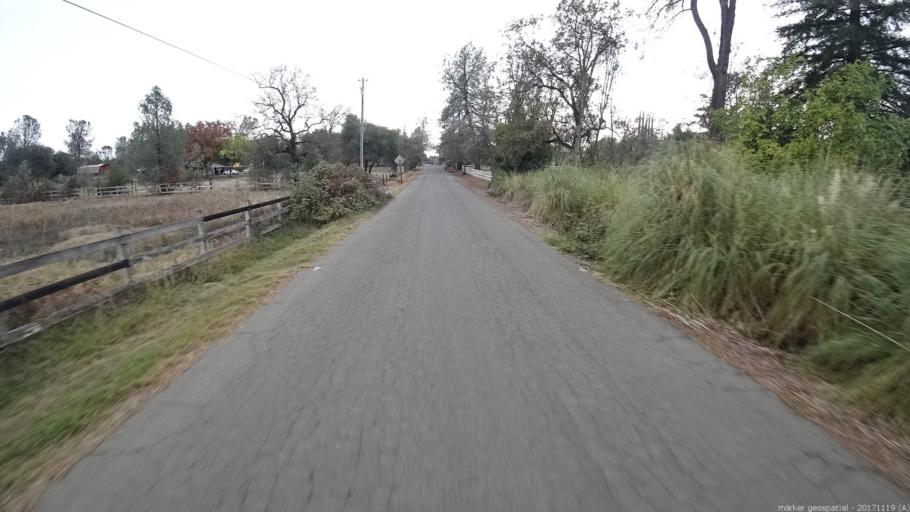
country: US
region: California
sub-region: Shasta County
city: Shasta
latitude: 40.4833
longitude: -122.4641
